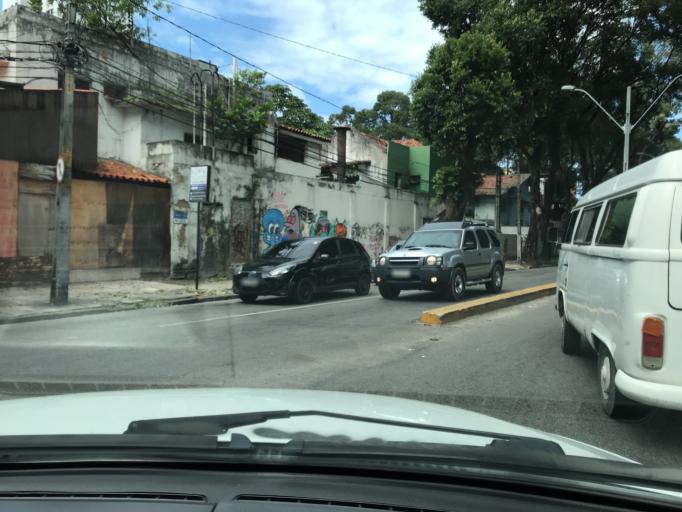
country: BR
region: Pernambuco
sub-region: Recife
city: Recife
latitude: -8.0576
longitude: -34.9001
